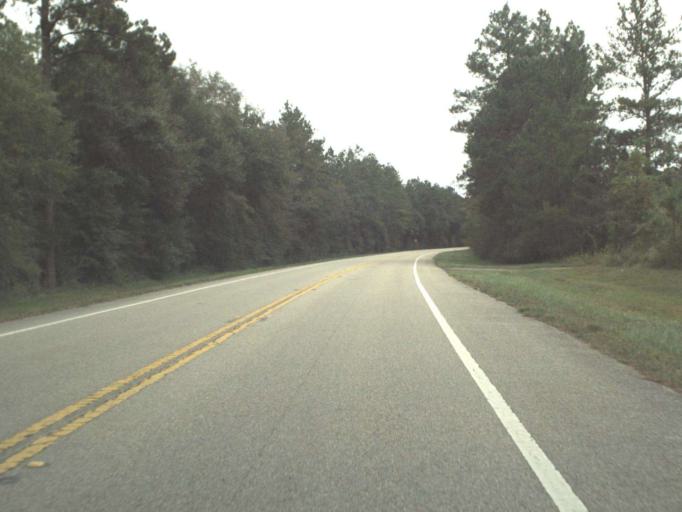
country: US
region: Florida
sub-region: Jackson County
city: Marianna
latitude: 30.6296
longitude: -85.1840
